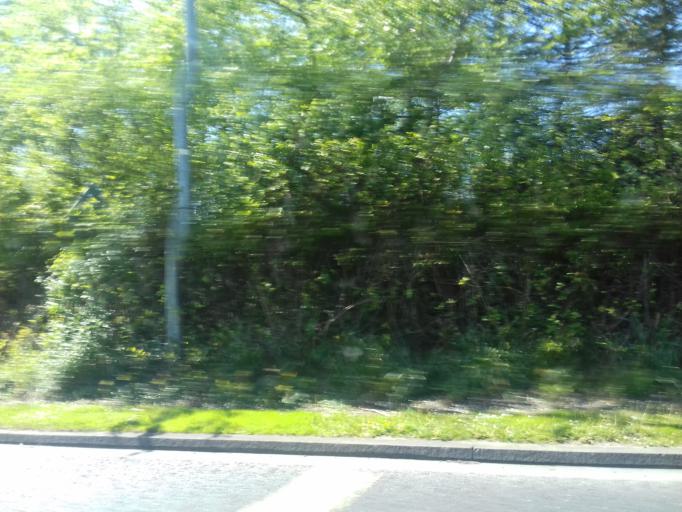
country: IE
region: Leinster
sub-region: Dublin City
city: Finglas
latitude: 53.3951
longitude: -6.3052
